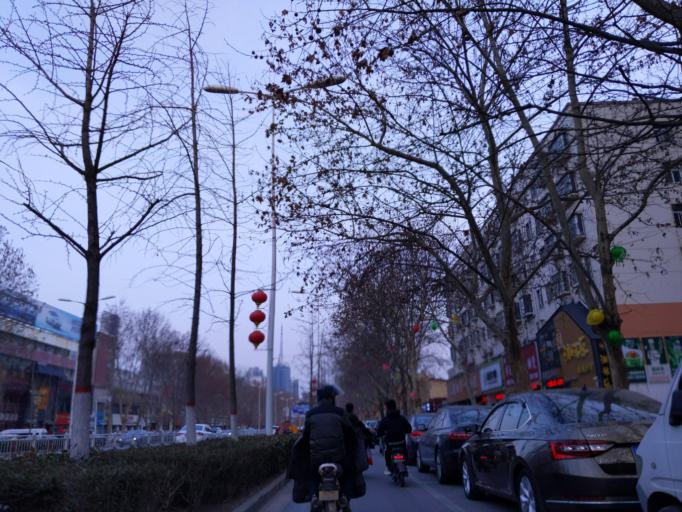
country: CN
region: Henan Sheng
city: Puyang
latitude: 35.7805
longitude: 115.0346
